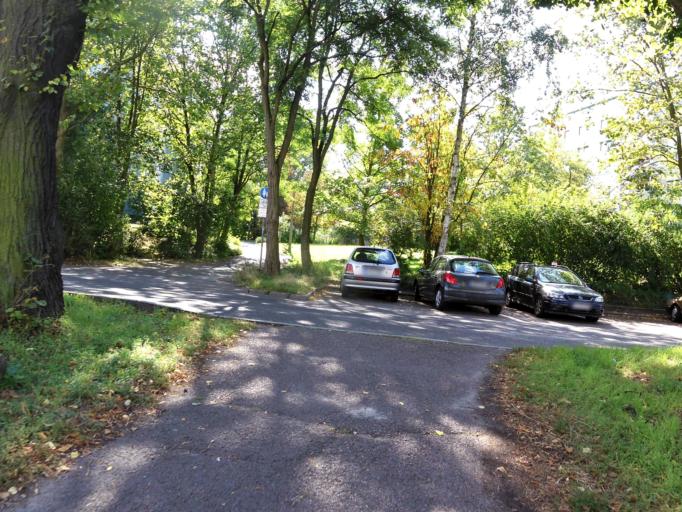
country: DE
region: Saxony
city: Taucha
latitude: 51.3795
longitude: 12.4345
